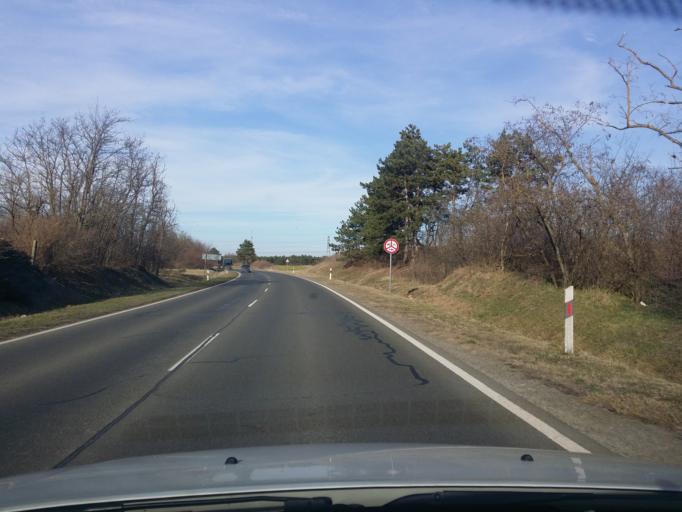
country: HU
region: Tolna
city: Dunaszentgyorgy
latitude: 46.5660
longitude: 18.8298
